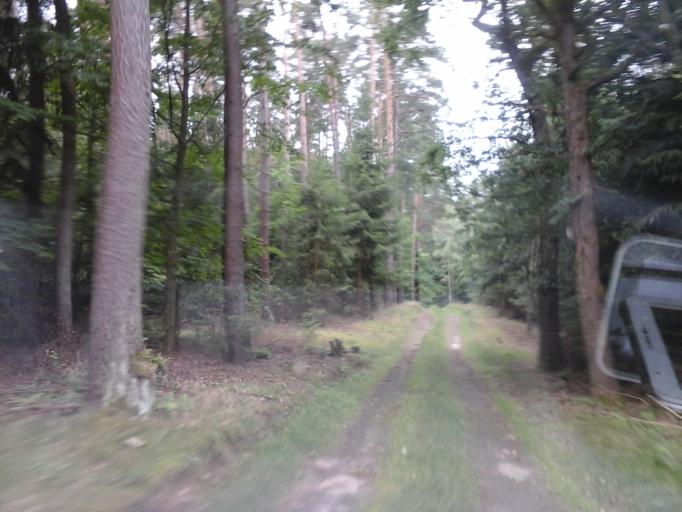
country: PL
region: West Pomeranian Voivodeship
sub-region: Powiat choszczenski
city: Pelczyce
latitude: 52.9577
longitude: 15.3544
